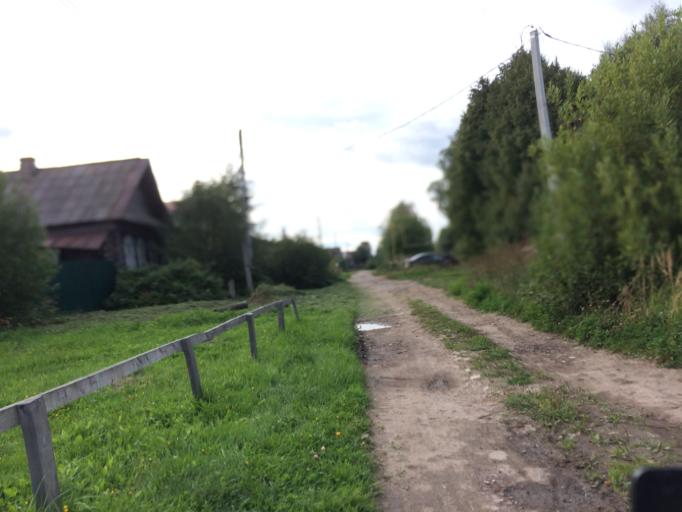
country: RU
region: Mariy-El
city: Yoshkar-Ola
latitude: 56.6518
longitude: 48.0169
